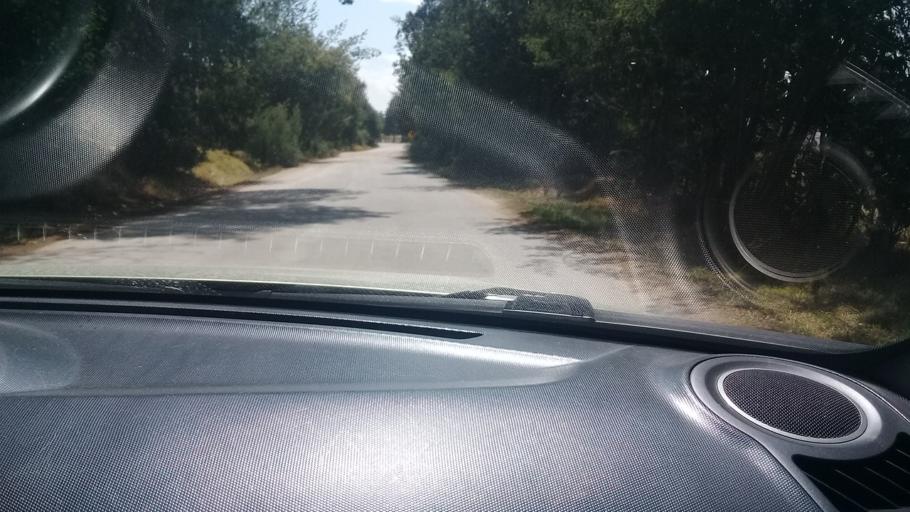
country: CO
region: Boyaca
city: Siachoque
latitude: 5.5517
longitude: -73.2921
